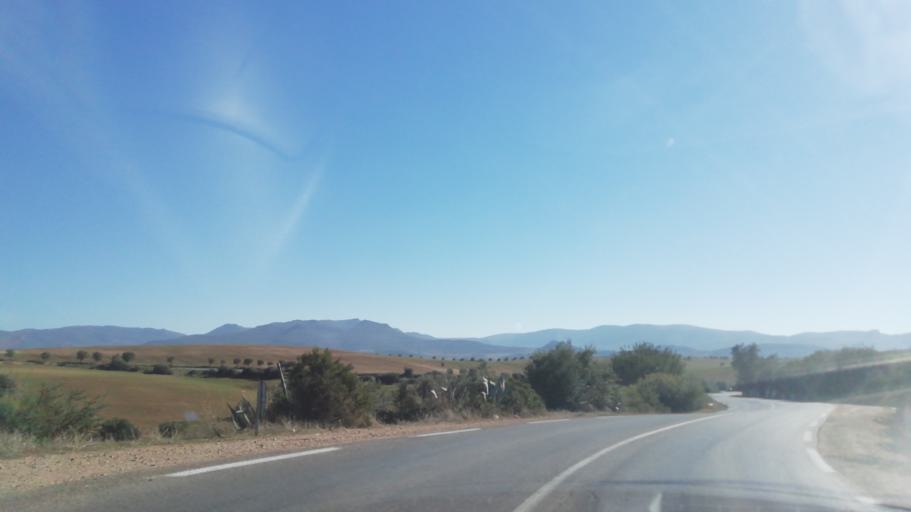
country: DZ
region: Tlemcen
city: Beni Mester
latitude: 34.8281
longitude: -1.5871
